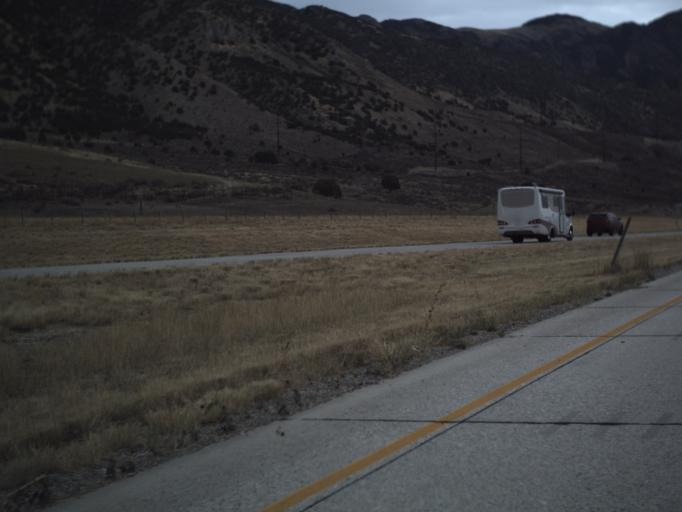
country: US
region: Idaho
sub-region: Oneida County
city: Malad City
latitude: 41.9749
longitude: -112.1890
